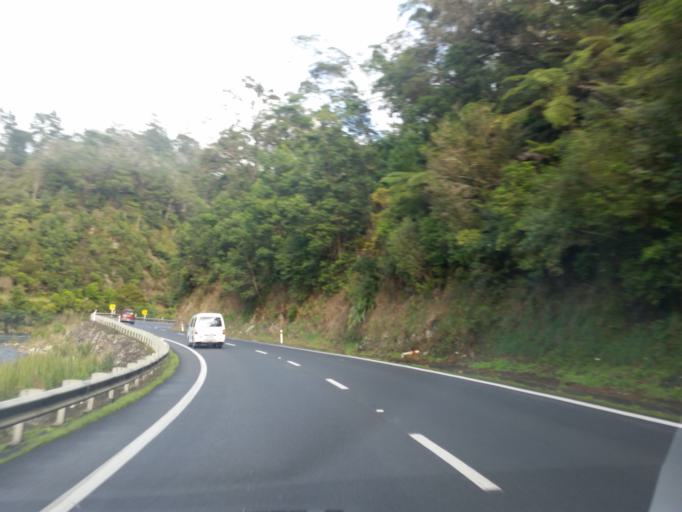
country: NZ
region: Waikato
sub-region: Hauraki District
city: Paeroa
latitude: -37.4186
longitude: 175.7424
